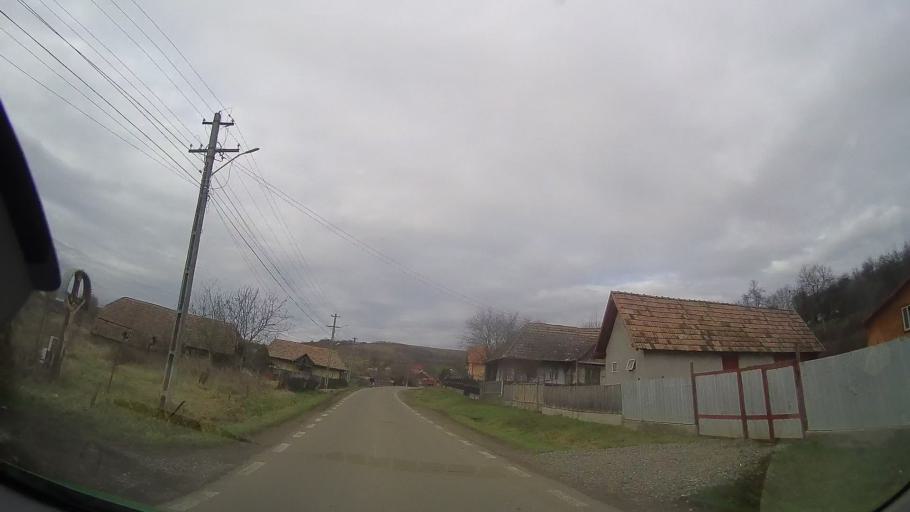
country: RO
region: Mures
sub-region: Comuna Cozma
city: Cozma
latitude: 46.8109
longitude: 24.5140
